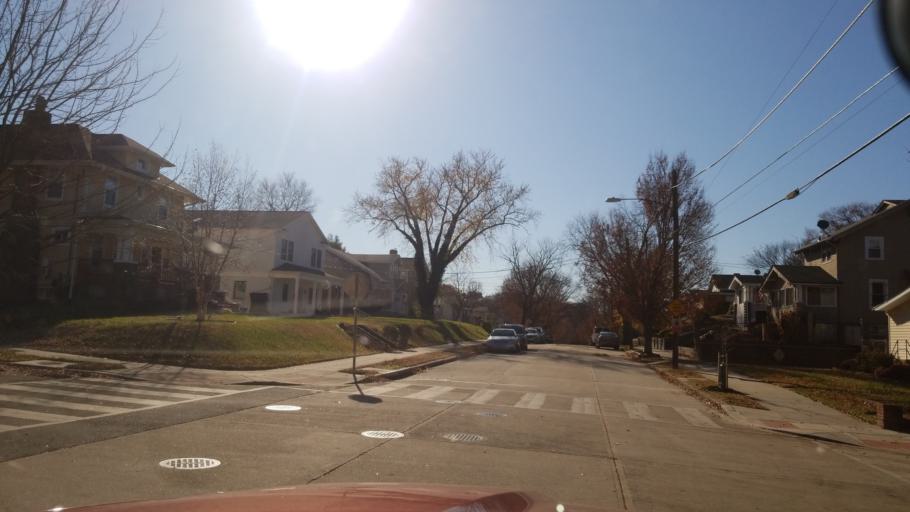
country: US
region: Maryland
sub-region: Prince George's County
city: Mount Rainier
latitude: 38.9309
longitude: -76.9624
